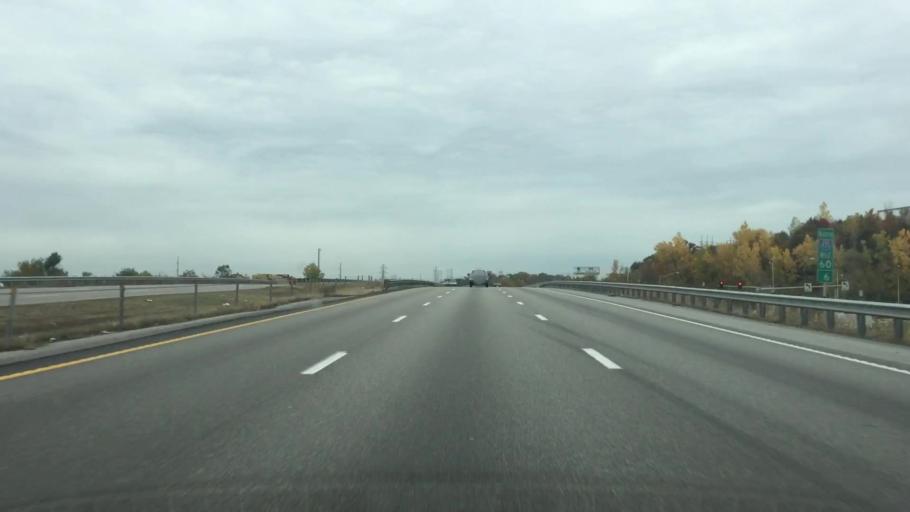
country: US
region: Missouri
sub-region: Jackson County
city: Sugar Creek
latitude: 39.0916
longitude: -94.4874
